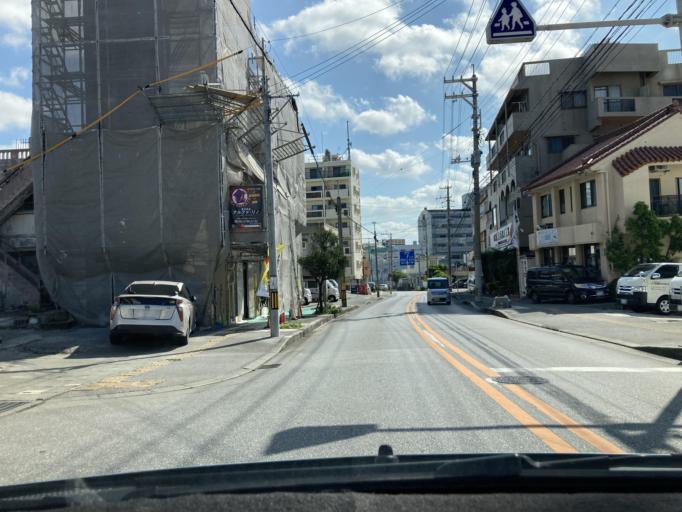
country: JP
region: Okinawa
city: Tomigusuku
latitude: 26.1945
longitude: 127.6745
